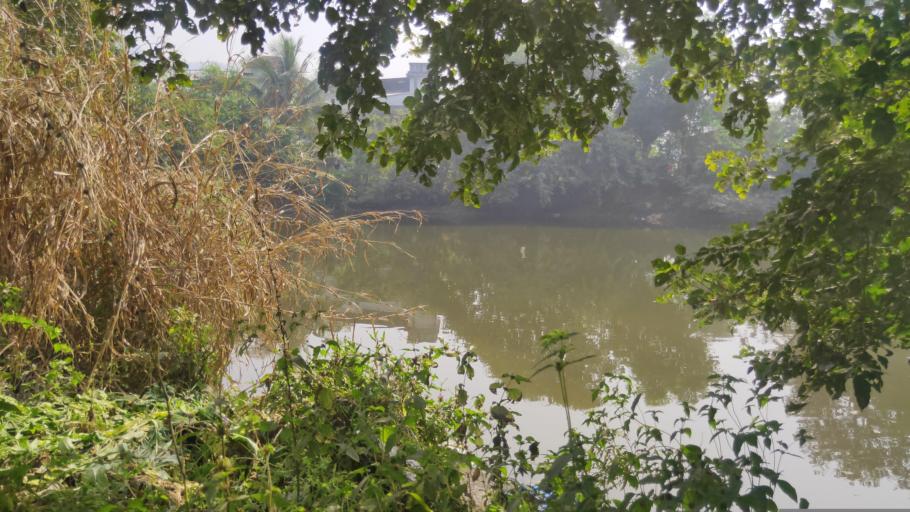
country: IN
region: Maharashtra
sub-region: Thane
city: Bhiwandi
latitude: 19.3119
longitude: 73.0881
